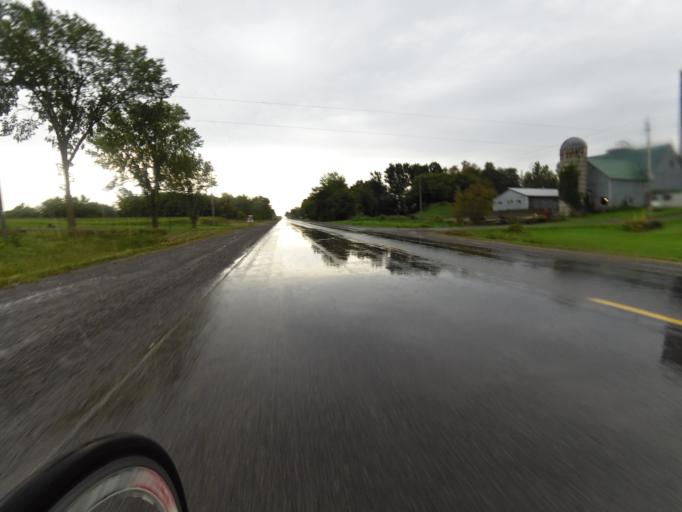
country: CA
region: Ontario
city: Bells Corners
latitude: 45.1773
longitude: -75.7181
